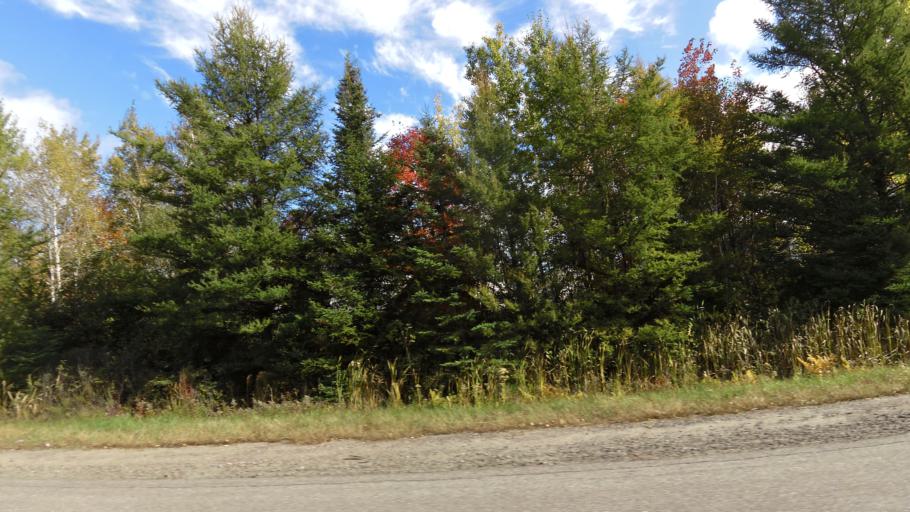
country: CA
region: Ontario
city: Deep River
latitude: 46.0269
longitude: -77.4586
